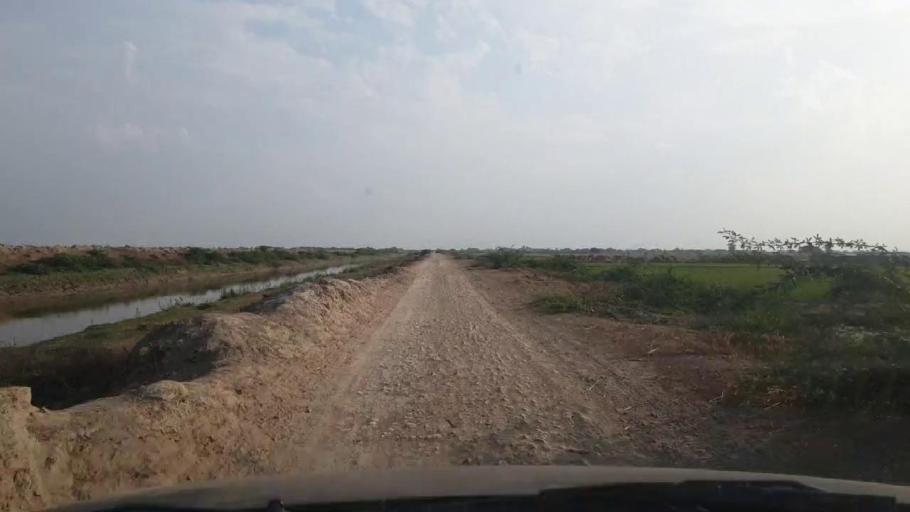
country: PK
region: Sindh
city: Badin
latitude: 24.5594
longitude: 68.6688
